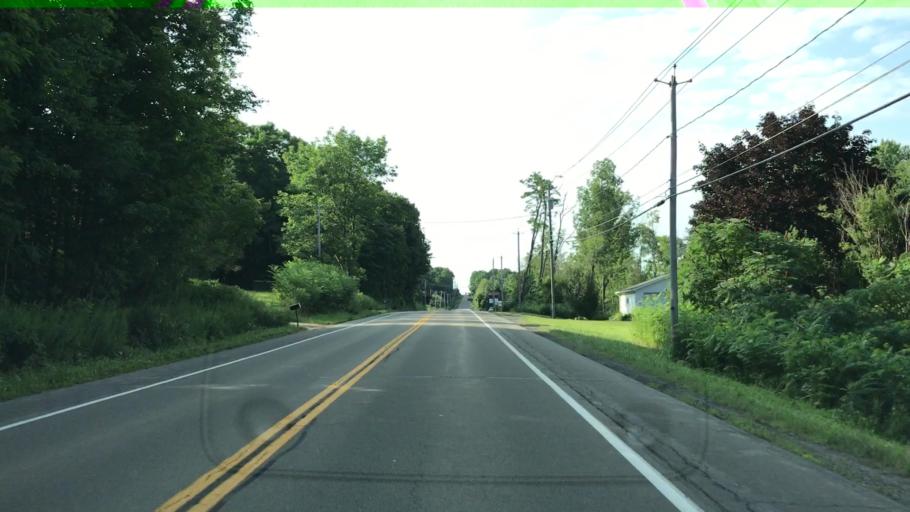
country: US
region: New York
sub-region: Chautauqua County
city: Mayville
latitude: 42.2557
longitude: -79.4671
